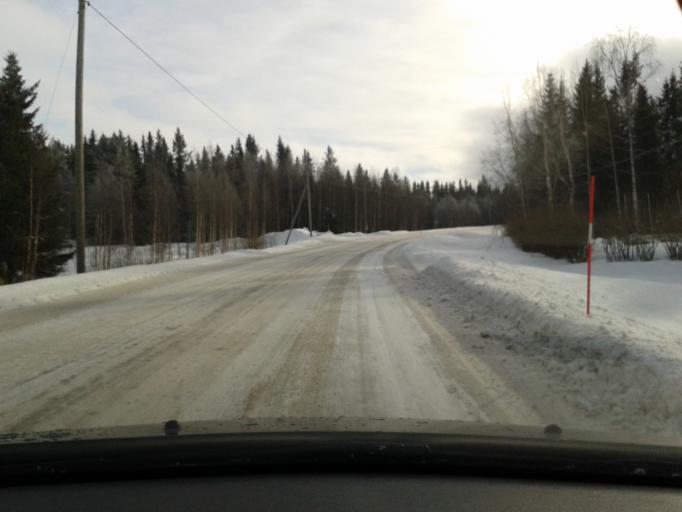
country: SE
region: Vaesterbotten
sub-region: Vilhelmina Kommun
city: Sjoberg
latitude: 64.6842
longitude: 16.2855
